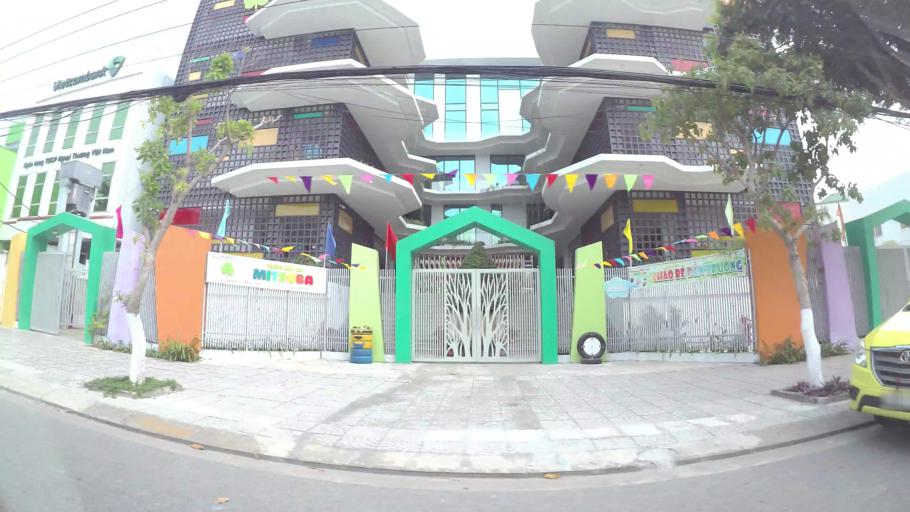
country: VN
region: Da Nang
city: Da Nang
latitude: 16.0810
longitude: 108.2353
